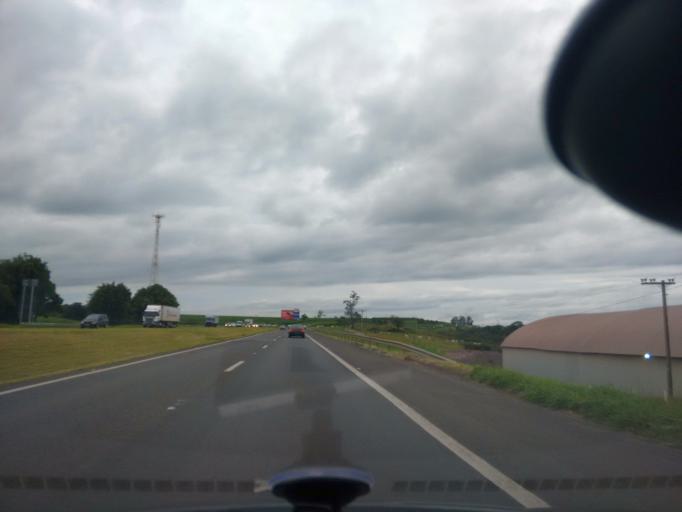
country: BR
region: Sao Paulo
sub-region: Rio Claro
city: Rio Claro
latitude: -22.3500
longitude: -47.6490
